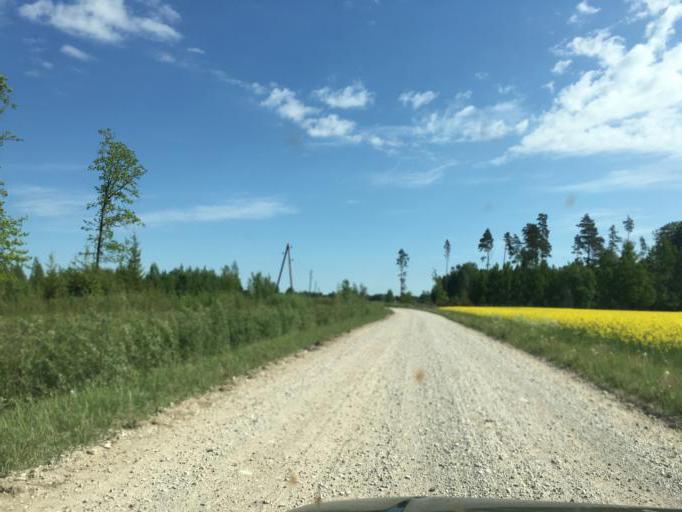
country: LV
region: Talsu Rajons
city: Valdemarpils
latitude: 57.3343
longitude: 22.4757
